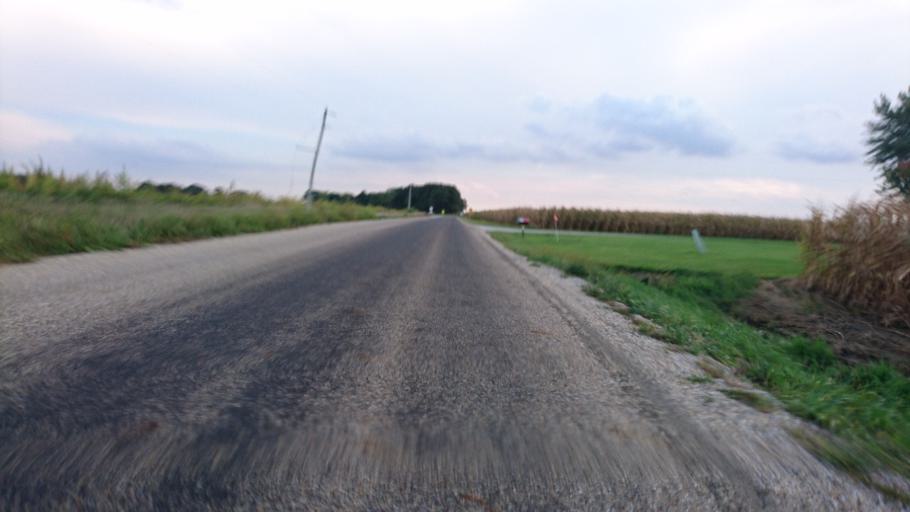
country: US
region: Illinois
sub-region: Logan County
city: Atlanta
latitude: 40.2328
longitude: -89.2049
